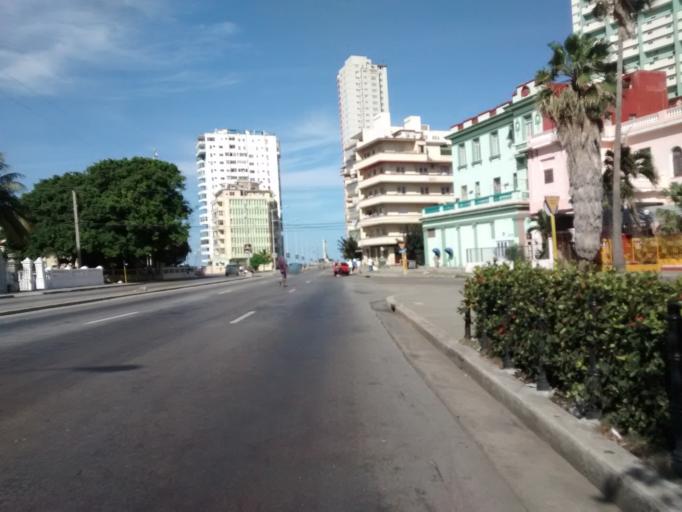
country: CU
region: La Habana
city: Havana
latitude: 23.1437
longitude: -82.3862
